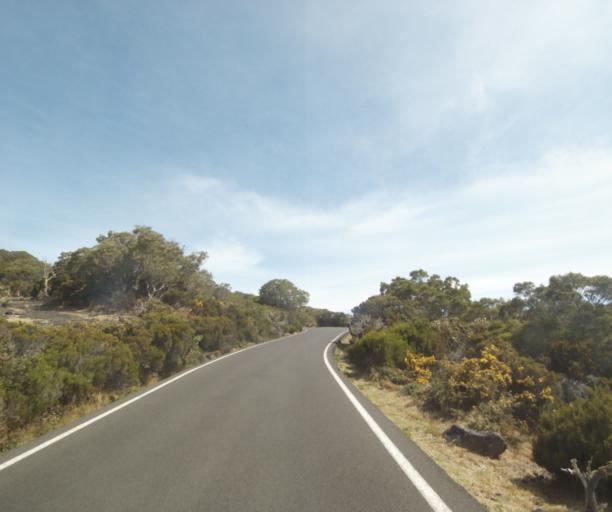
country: RE
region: Reunion
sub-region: Reunion
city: Trois-Bassins
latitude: -21.0635
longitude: 55.3785
